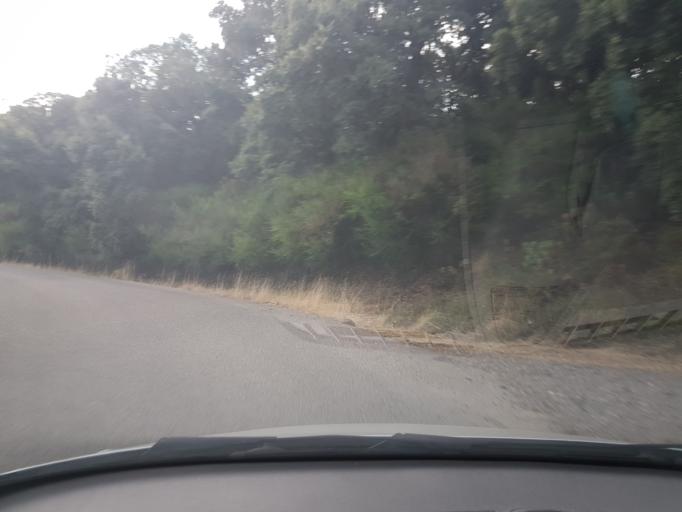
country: IT
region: Sardinia
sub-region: Provincia di Oristano
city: Seneghe
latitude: 40.1113
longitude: 8.6195
